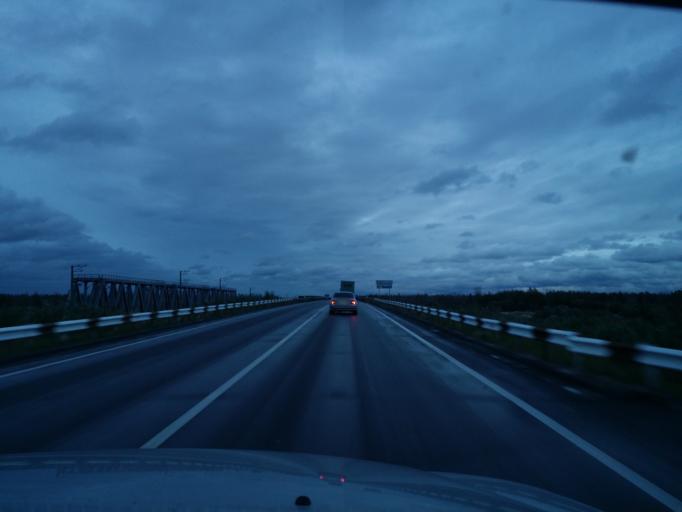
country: RU
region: Khanty-Mansiyskiy Avtonomnyy Okrug
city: Lokosovo
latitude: 61.4564
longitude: 74.6690
